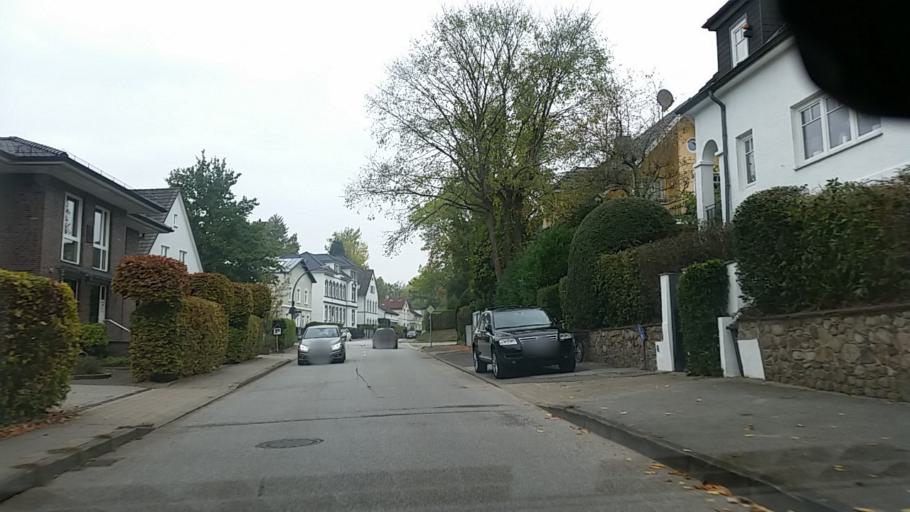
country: DE
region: Schleswig-Holstein
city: Halstenbek
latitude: 53.5594
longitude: 9.8465
